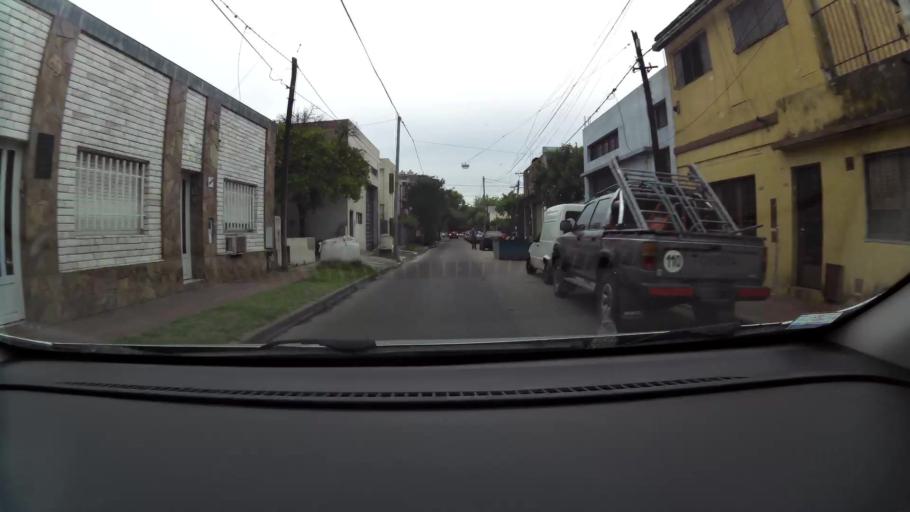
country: AR
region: Santa Fe
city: Granadero Baigorria
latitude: -32.9062
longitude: -60.6934
